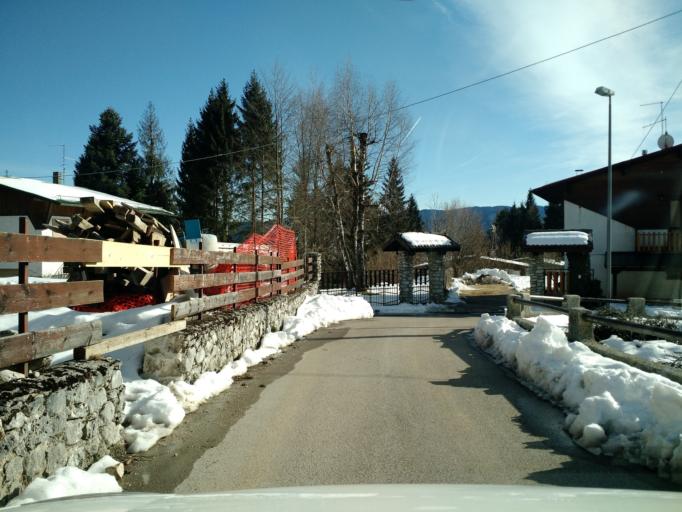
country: IT
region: Veneto
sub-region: Provincia di Vicenza
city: Roana
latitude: 45.8824
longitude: 11.4674
